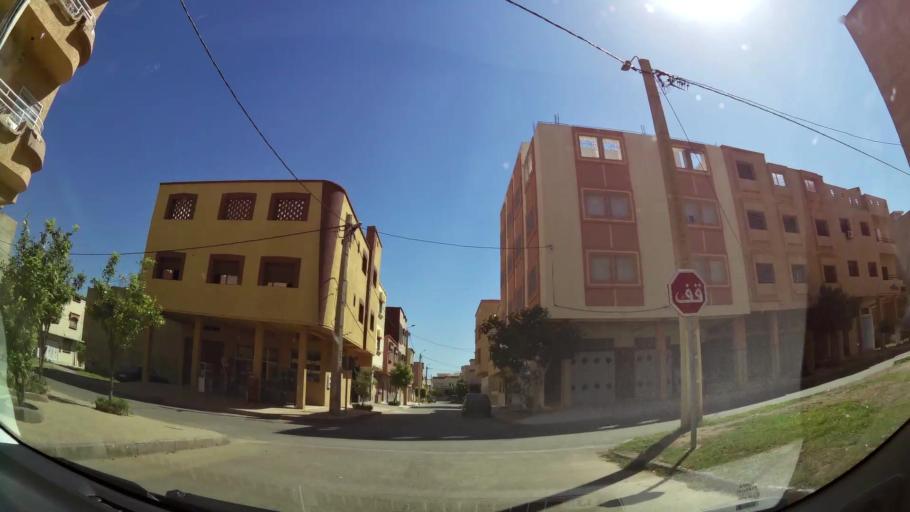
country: MA
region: Oriental
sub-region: Oujda-Angad
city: Oujda
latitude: 34.6572
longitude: -1.8897
